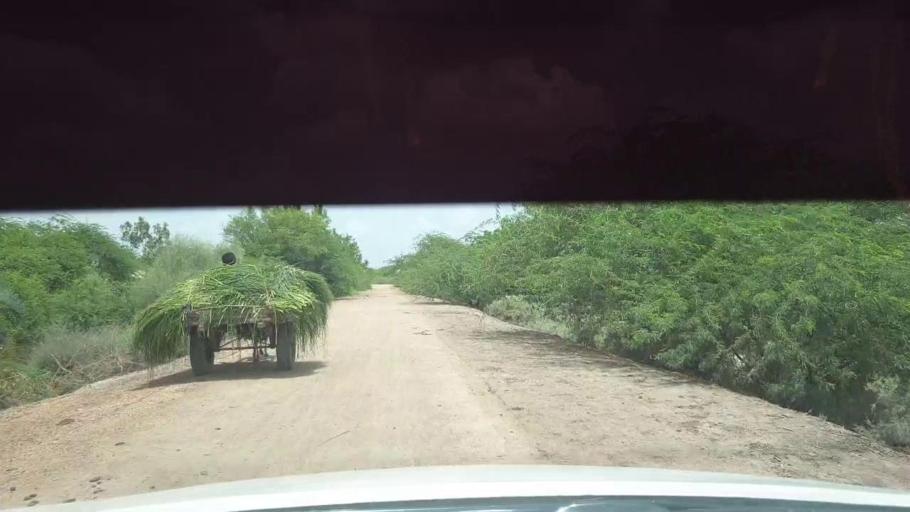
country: PK
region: Sindh
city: Kadhan
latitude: 24.4835
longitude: 69.0028
